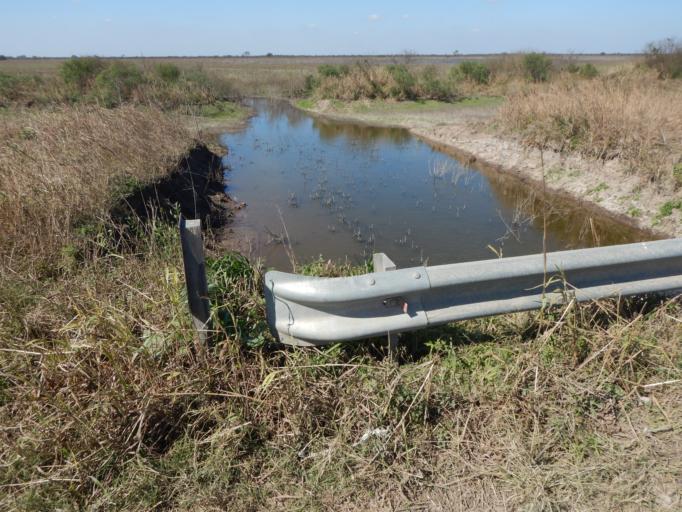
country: AR
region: Santiago del Estero
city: Los Juries
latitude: -28.6399
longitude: -61.5246
